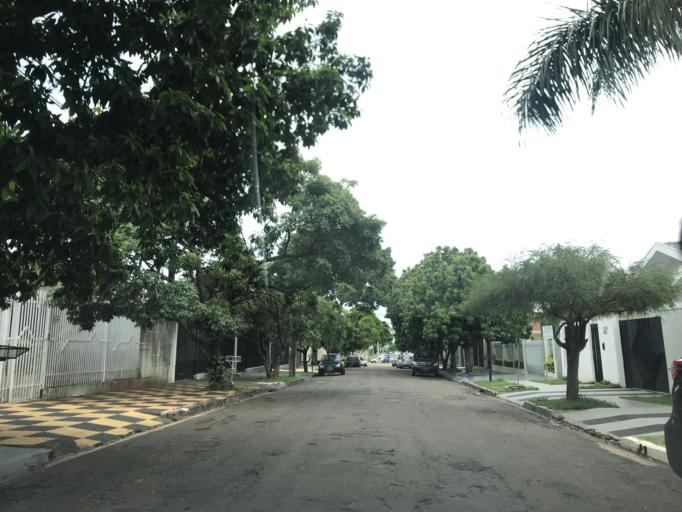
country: BR
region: Parana
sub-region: Maringa
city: Maringa
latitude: -23.4481
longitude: -51.9558
